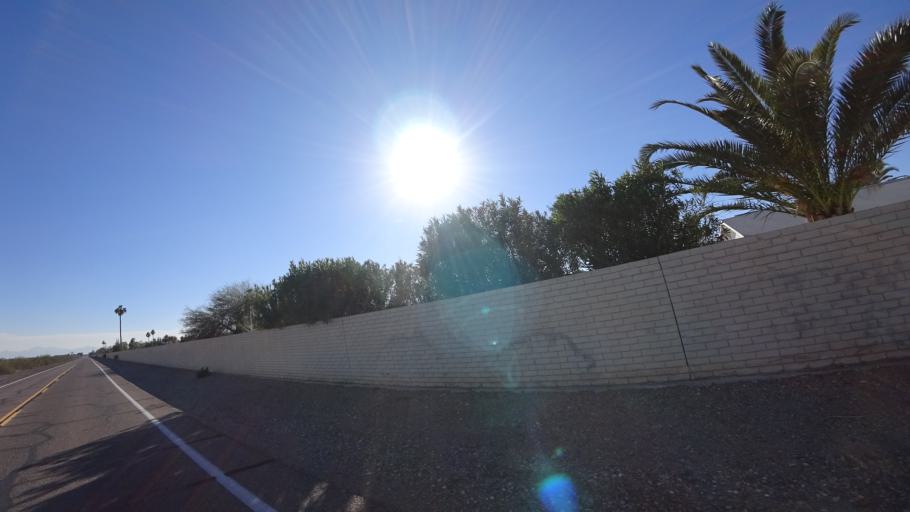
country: US
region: Arizona
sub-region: Maricopa County
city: Sun City West
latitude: 33.6544
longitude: -112.3251
